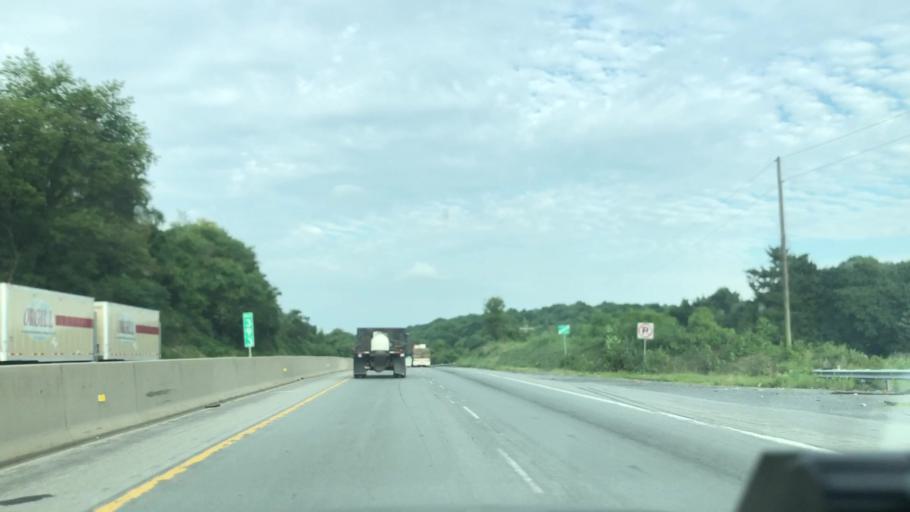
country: US
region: Pennsylvania
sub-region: Berks County
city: Kutztown
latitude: 40.5791
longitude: -75.8205
